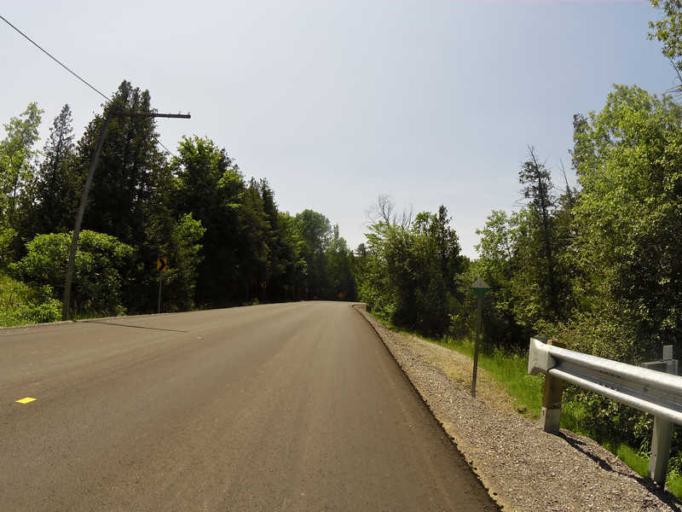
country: CA
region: Ontario
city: Peterborough
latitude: 44.3722
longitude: -78.2858
